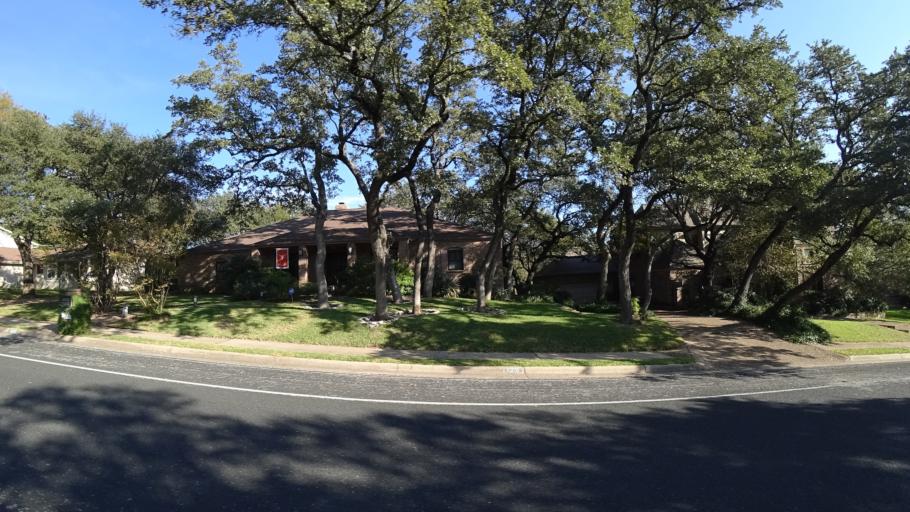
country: US
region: Texas
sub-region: Williamson County
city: Anderson Mill
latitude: 30.4409
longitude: -97.8100
